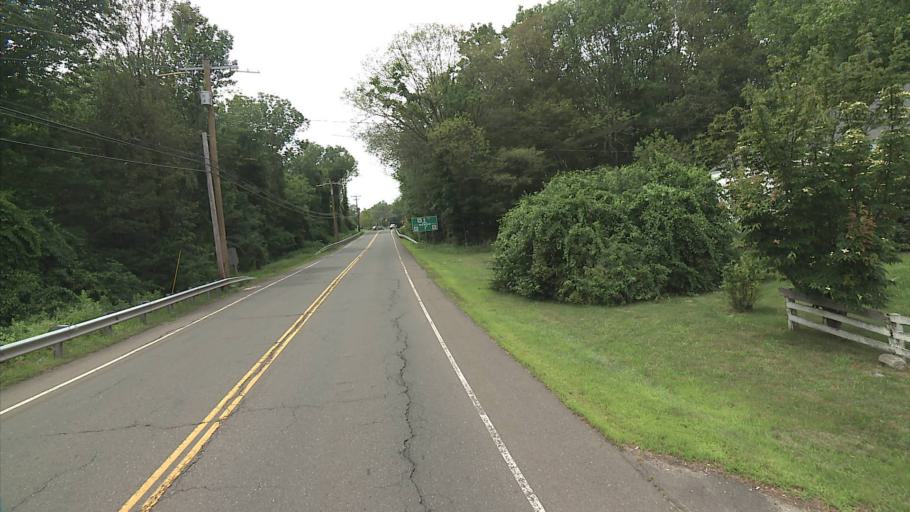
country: US
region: Connecticut
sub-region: Middlesex County
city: Clinton
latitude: 41.3573
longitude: -72.5618
